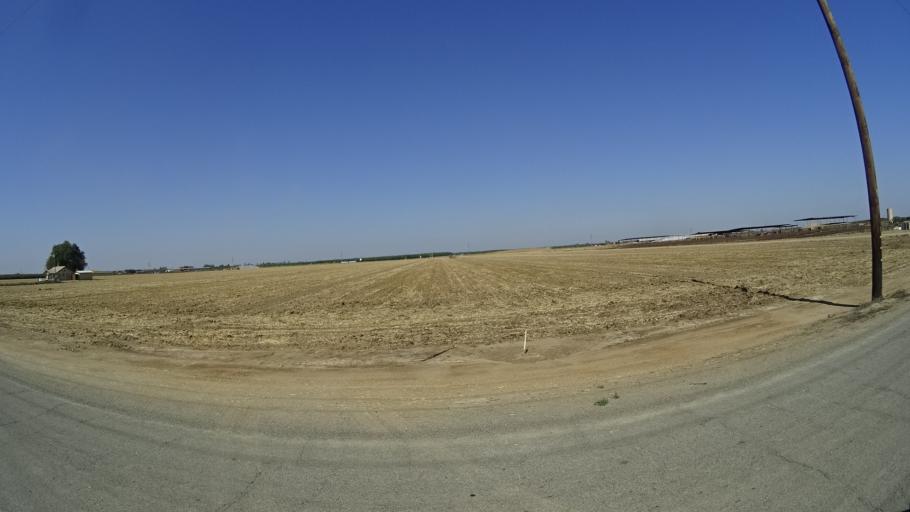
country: US
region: California
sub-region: Kings County
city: Hanford
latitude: 36.3647
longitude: -119.5830
